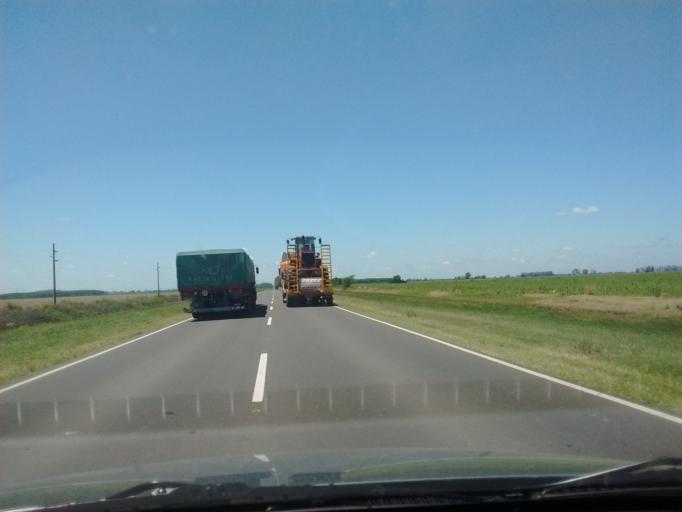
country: AR
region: Entre Rios
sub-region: Departamento de Gualeguay
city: Gualeguay
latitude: -33.0795
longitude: -59.3952
